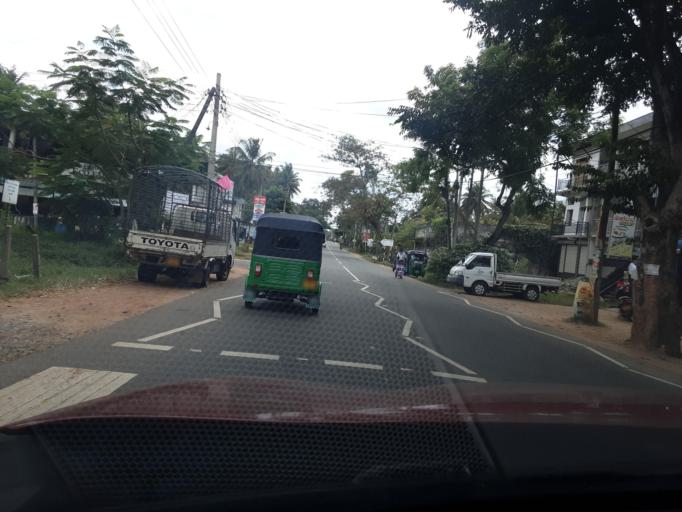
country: LK
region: North Western
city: Kuliyapitiya
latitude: 7.4514
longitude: 80.1685
